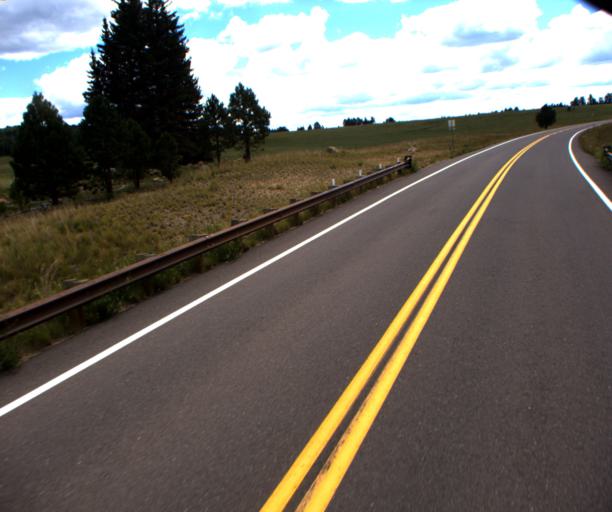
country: US
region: Arizona
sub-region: Apache County
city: Eagar
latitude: 33.9915
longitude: -109.5149
